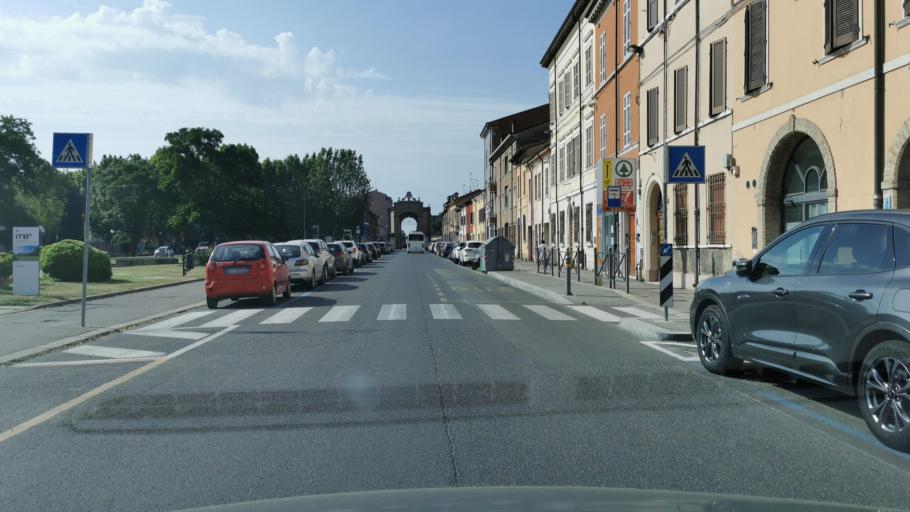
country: IT
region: Emilia-Romagna
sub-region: Provincia di Ravenna
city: Ravenna
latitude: 44.4138
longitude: 12.2057
